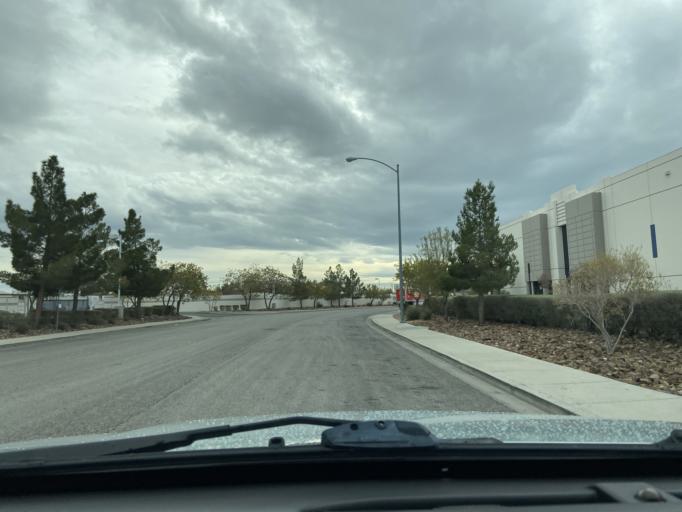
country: US
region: Nevada
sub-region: Clark County
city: Sunrise Manor
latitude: 36.2450
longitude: -115.1045
